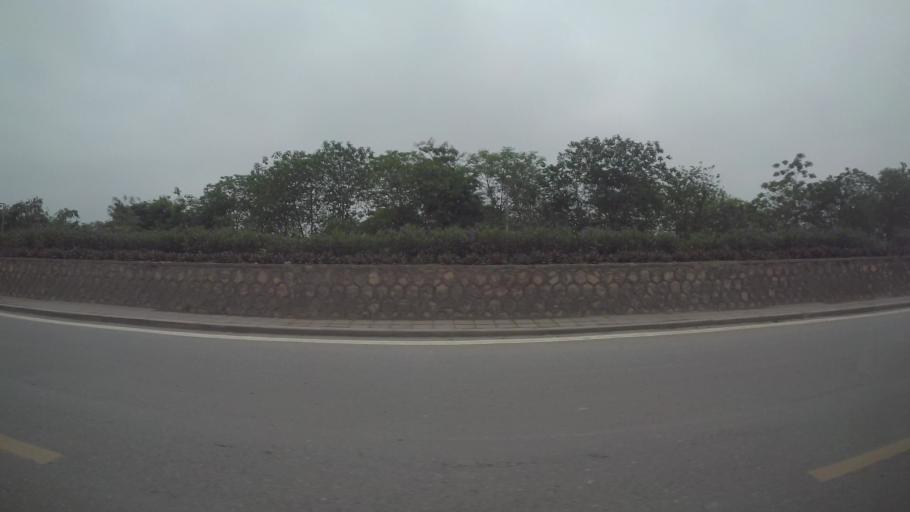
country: VN
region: Ha Noi
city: Trau Quy
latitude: 20.9843
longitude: 105.8950
